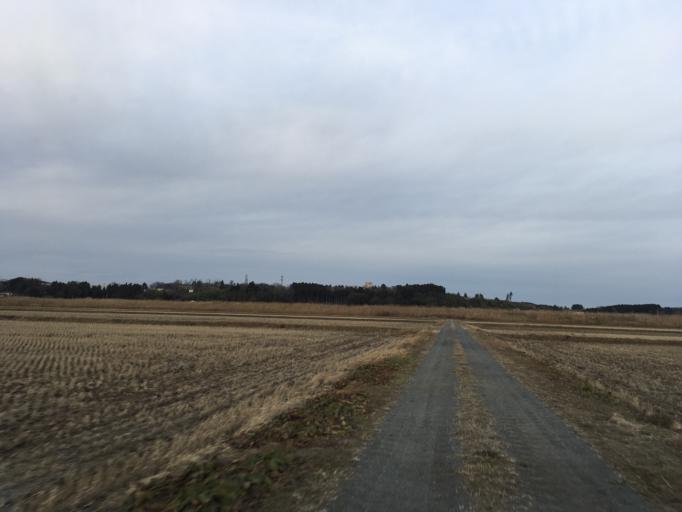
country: JP
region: Miyagi
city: Kogota
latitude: 38.6440
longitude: 141.0689
